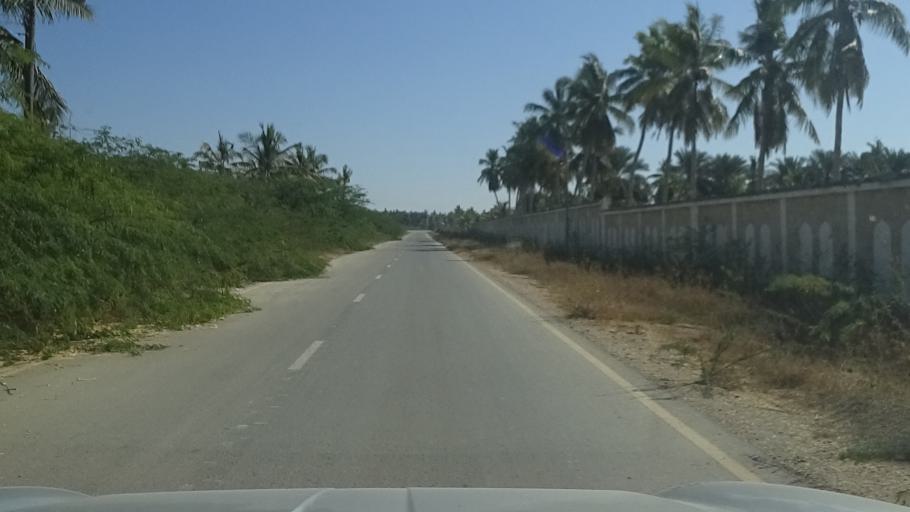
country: OM
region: Zufar
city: Salalah
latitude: 17.0329
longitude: 54.1487
